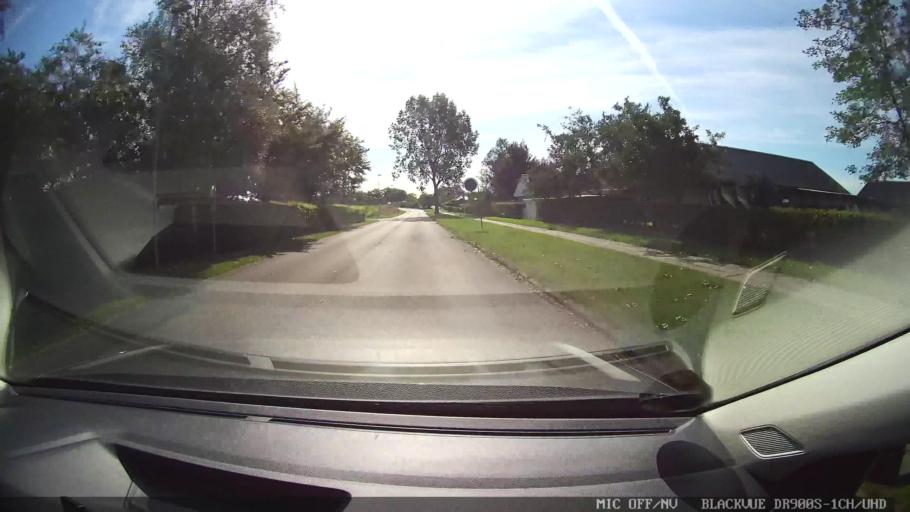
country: DK
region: North Denmark
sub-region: Mariagerfjord Kommune
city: Hobro
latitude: 56.5464
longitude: 9.8535
